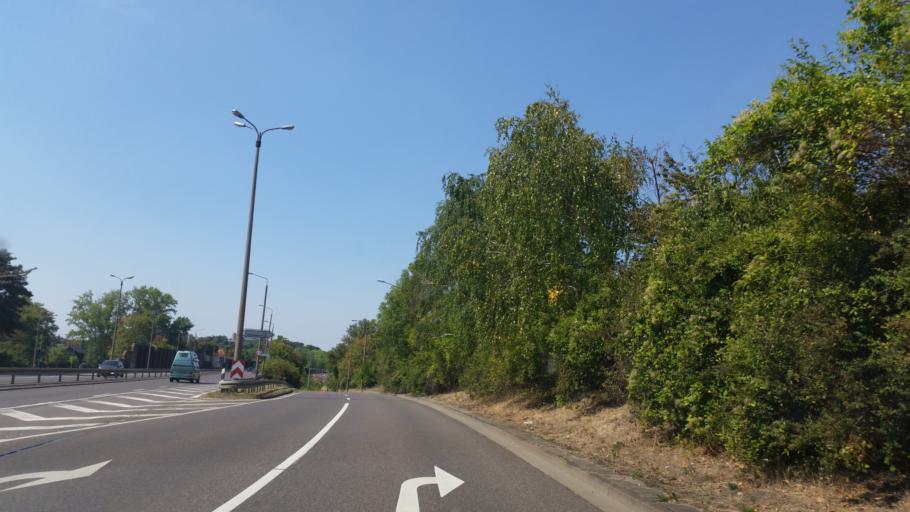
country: DE
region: Saxony-Anhalt
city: Halle (Saale)
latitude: 51.5007
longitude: 11.9770
